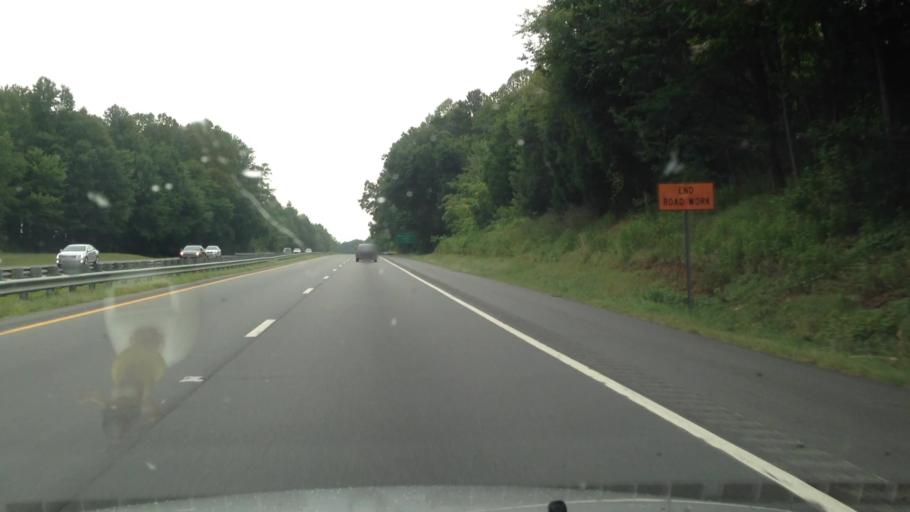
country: US
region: North Carolina
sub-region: Forsyth County
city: Kernersville
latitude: 36.0997
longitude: -80.0196
